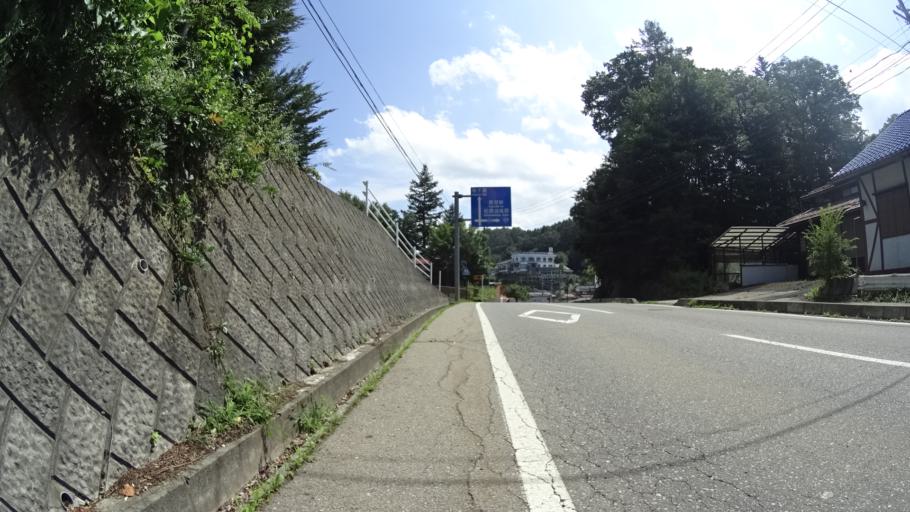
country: JP
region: Nagano
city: Saku
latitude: 36.0522
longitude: 138.4601
